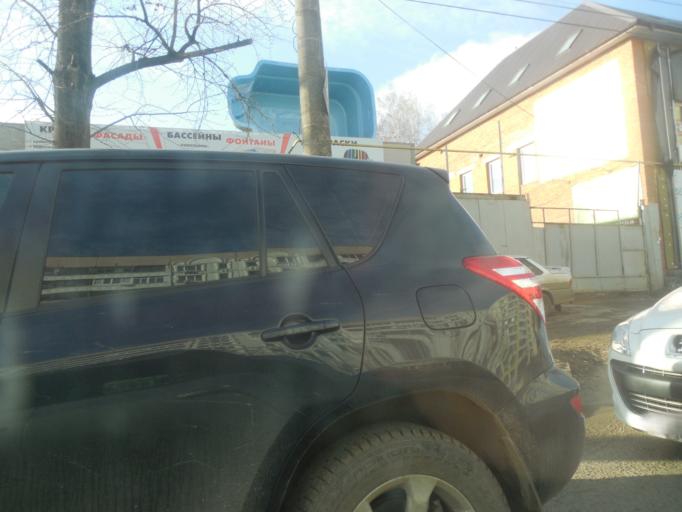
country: RU
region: Tula
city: Mendeleyevskiy
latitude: 54.1594
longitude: 37.6024
